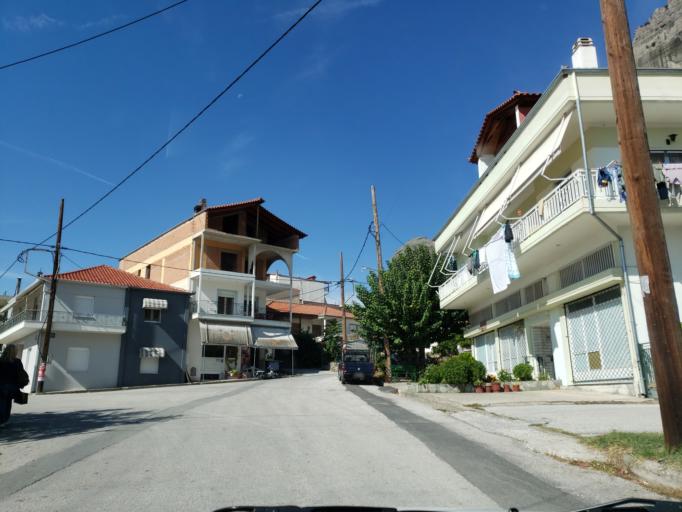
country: GR
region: Thessaly
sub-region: Trikala
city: Kalampaka
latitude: 39.7081
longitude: 21.6291
